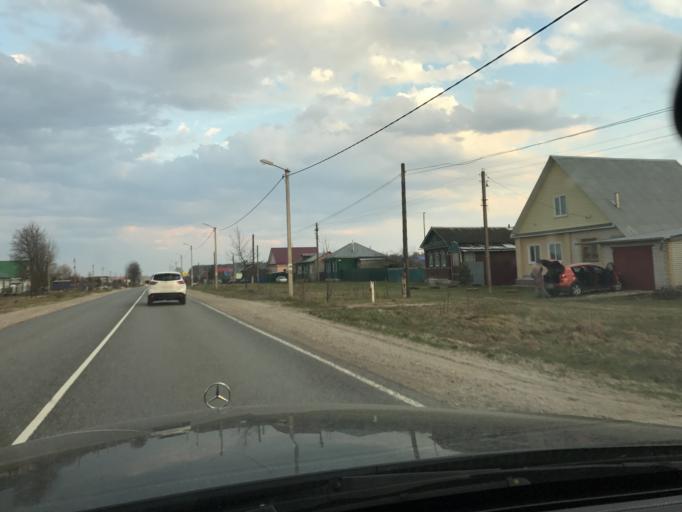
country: RU
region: Vladimir
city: Murom
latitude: 55.6070
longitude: 41.9595
